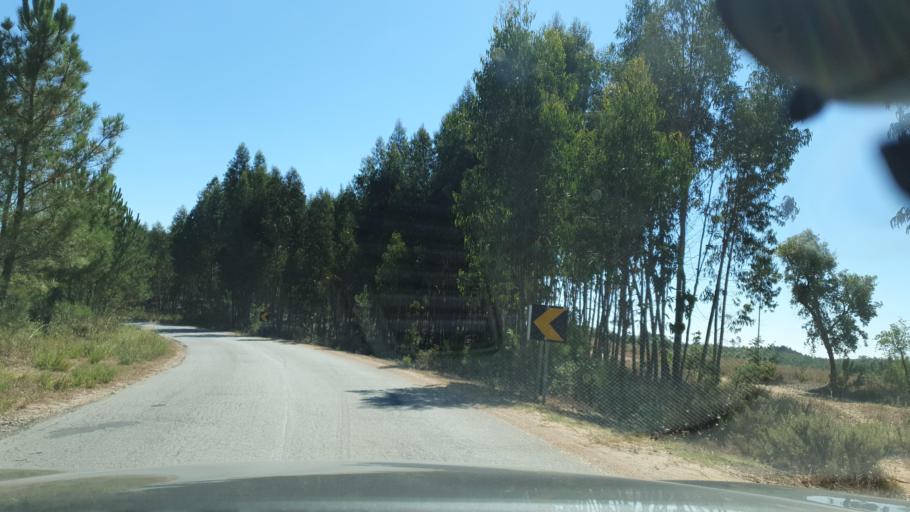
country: PT
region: Beja
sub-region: Odemira
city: Sao Teotonio
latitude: 37.4981
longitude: -8.6654
